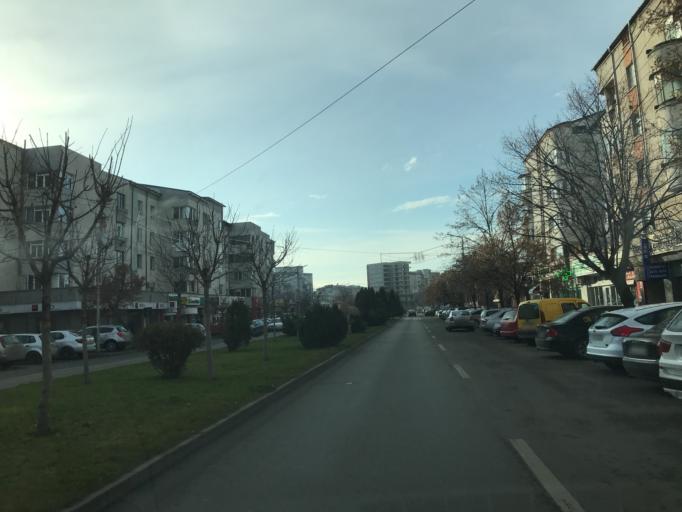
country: RO
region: Olt
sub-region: Municipiul Slatina
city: Slatina
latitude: 44.4270
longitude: 24.3788
